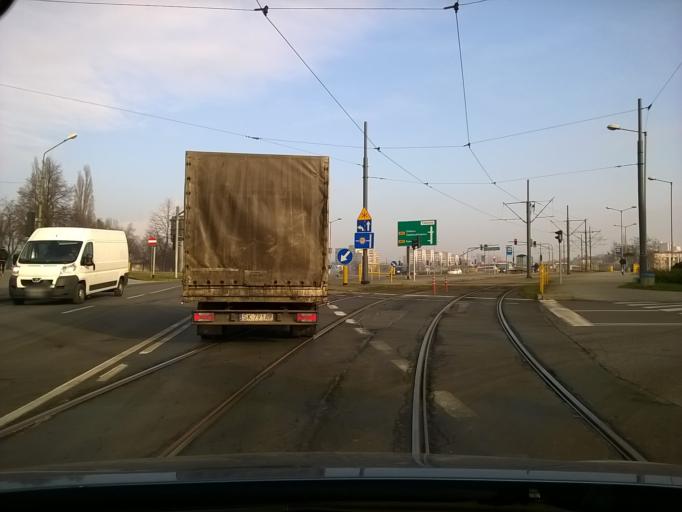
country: PL
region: Silesian Voivodeship
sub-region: Swietochlowice
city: Swietochlowice
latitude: 50.2807
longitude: 18.9458
